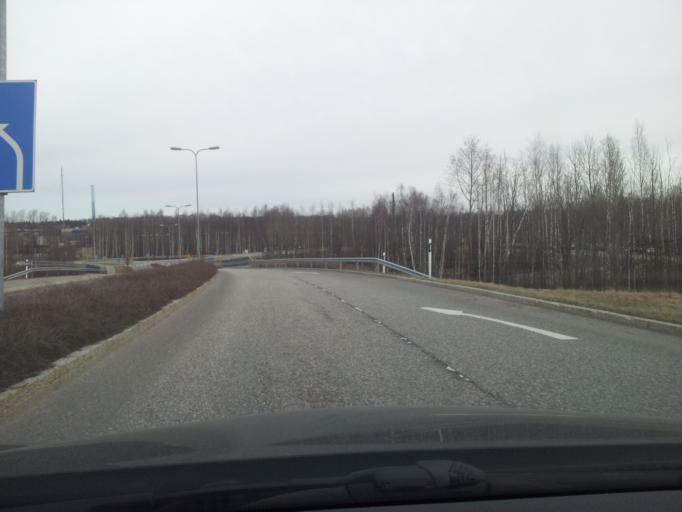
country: FI
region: Uusimaa
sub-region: Helsinki
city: Teekkarikylae
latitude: 60.2096
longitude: 24.8313
